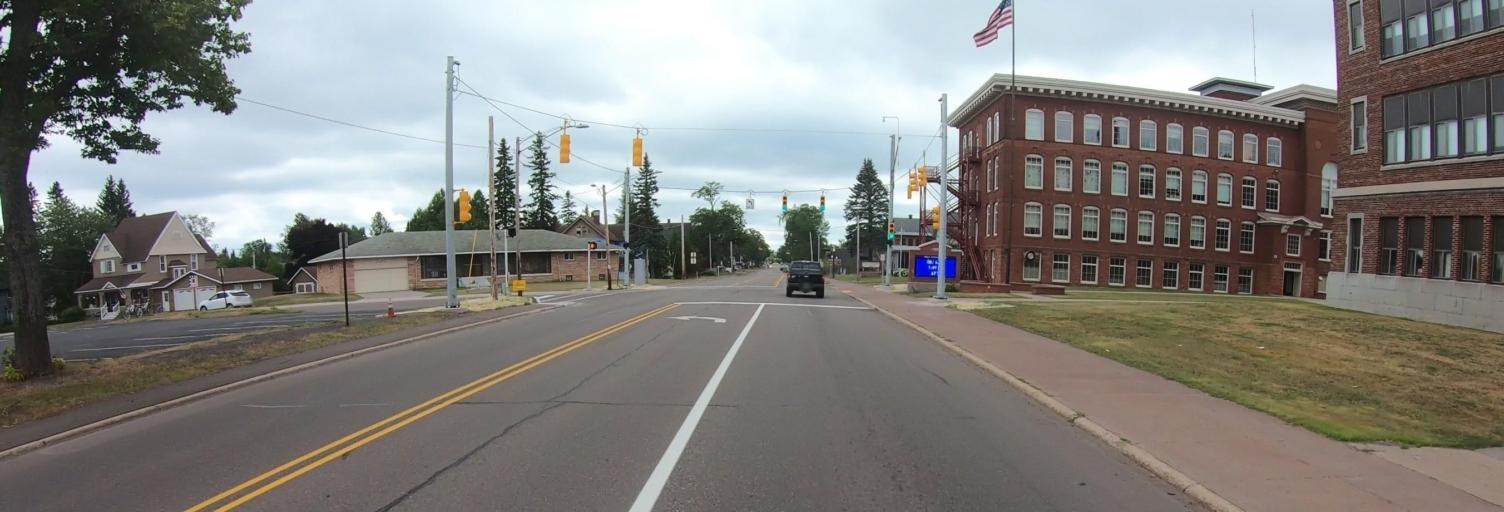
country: US
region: Michigan
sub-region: Houghton County
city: Laurium
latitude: 47.2436
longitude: -88.4461
